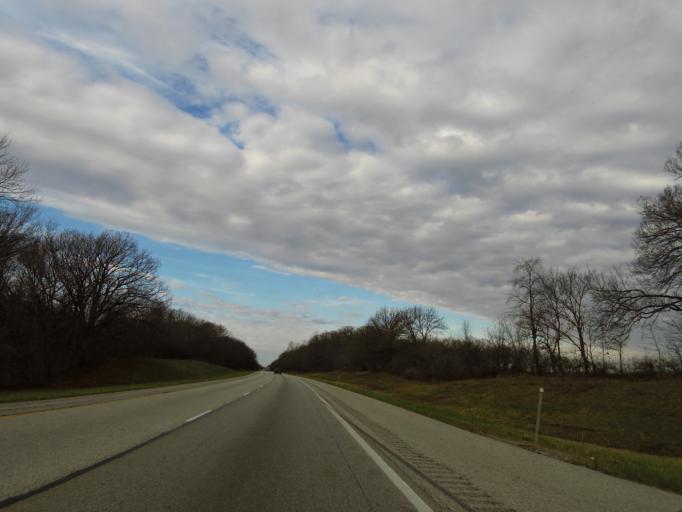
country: US
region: Illinois
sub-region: Washington County
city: Nashville
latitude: 38.4083
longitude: -89.4125
